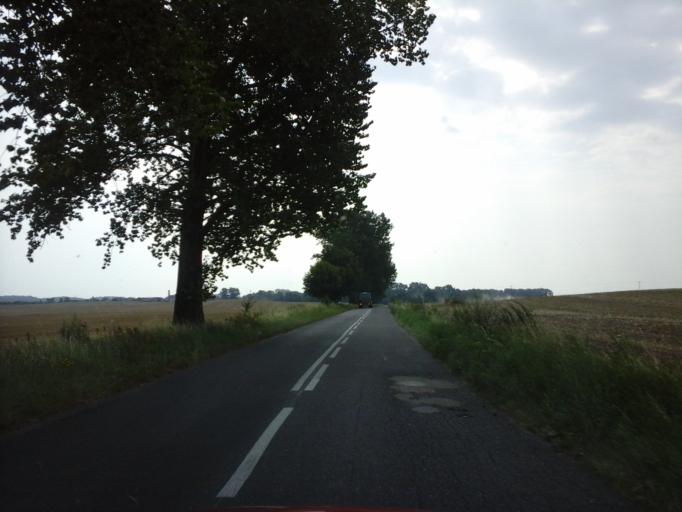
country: PL
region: West Pomeranian Voivodeship
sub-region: Powiat choszczenski
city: Pelczyce
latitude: 53.0543
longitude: 15.3664
